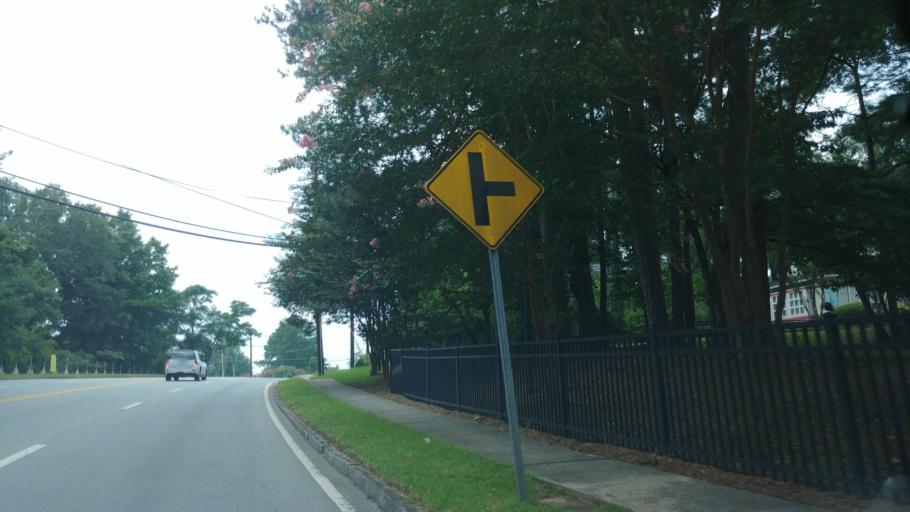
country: US
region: Georgia
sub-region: DeKalb County
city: Chamblee
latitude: 33.8778
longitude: -84.2875
